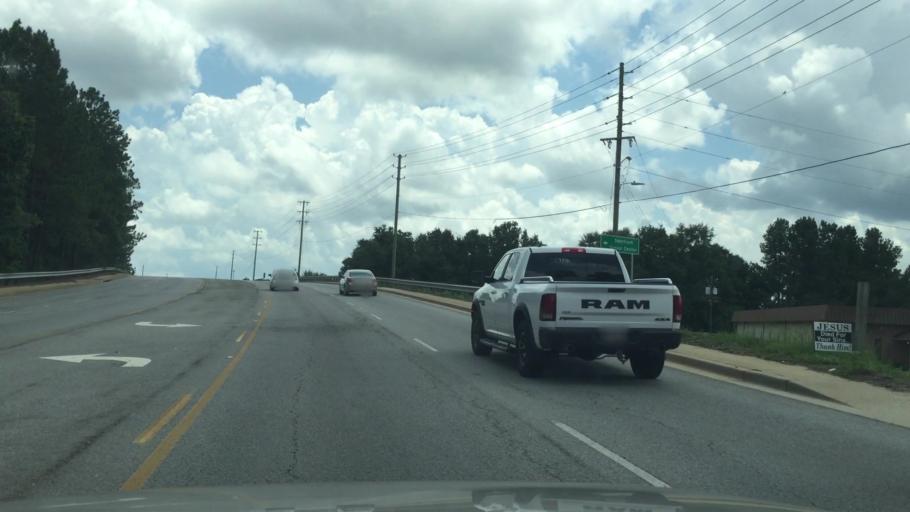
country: US
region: South Carolina
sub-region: Sumter County
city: South Sumter
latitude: 33.9101
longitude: -80.3820
